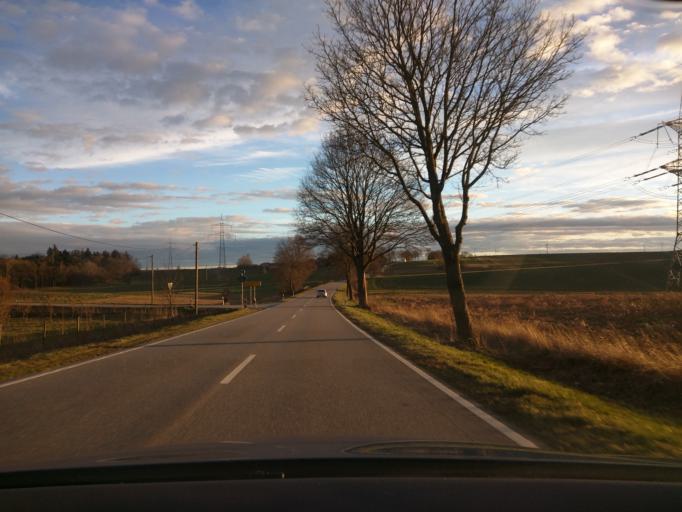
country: DE
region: Bavaria
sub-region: Upper Bavaria
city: Wolfersdorf
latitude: 48.5287
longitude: 11.7570
